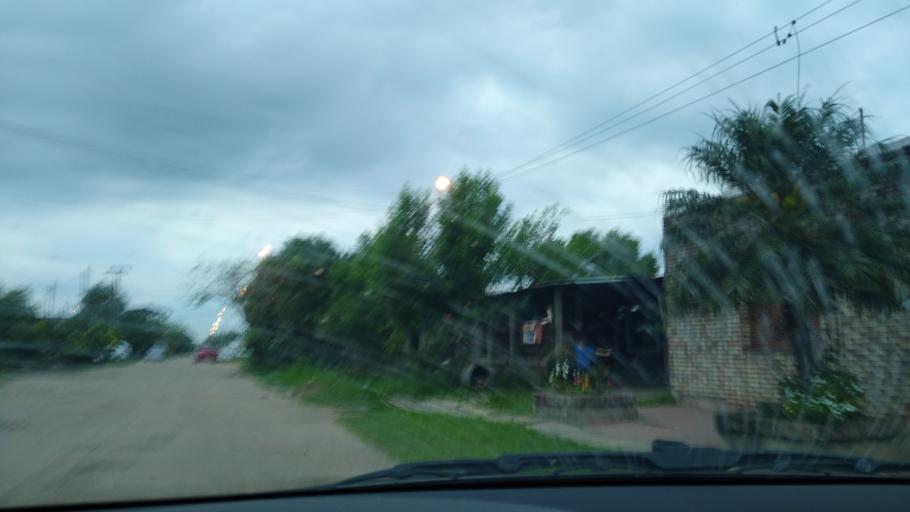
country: AR
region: Chaco
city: Barranqueras
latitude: -27.4870
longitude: -58.9369
